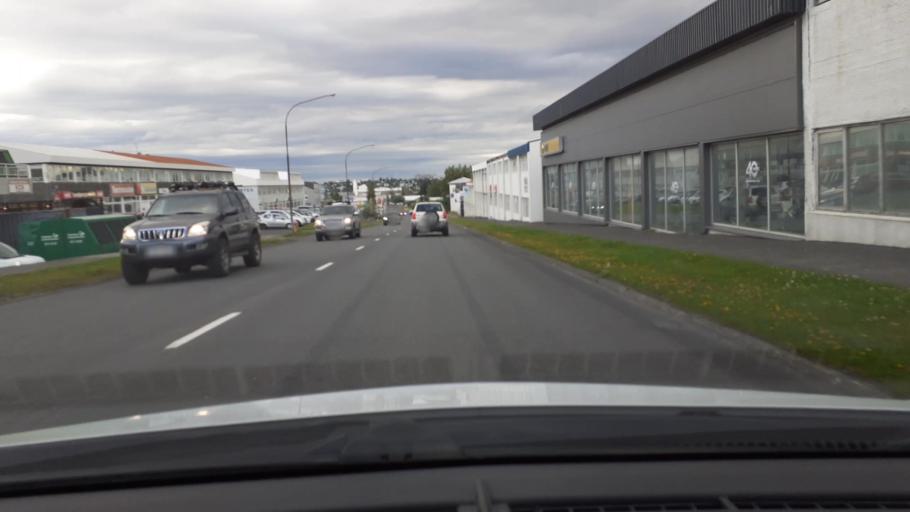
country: IS
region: Capital Region
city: Reykjavik
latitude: 64.1257
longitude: -21.8146
